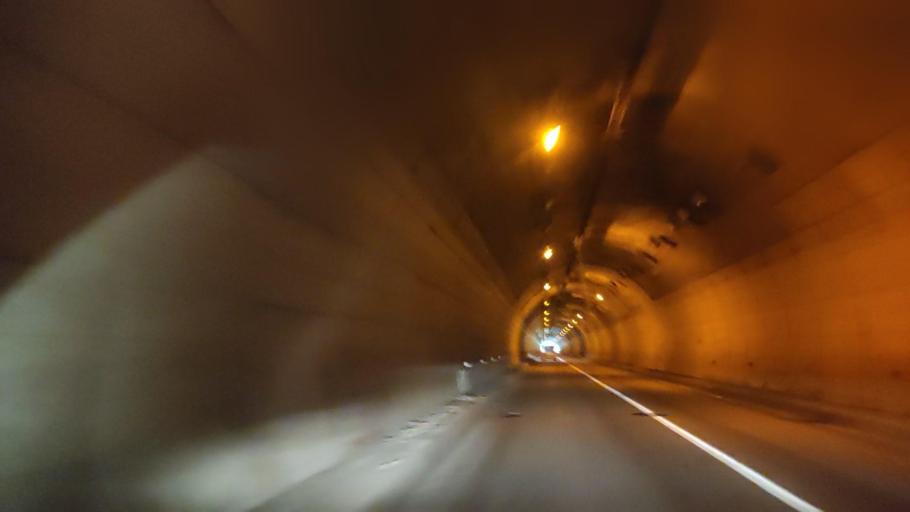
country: JP
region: Hokkaido
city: Bibai
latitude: 43.2885
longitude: 142.0724
